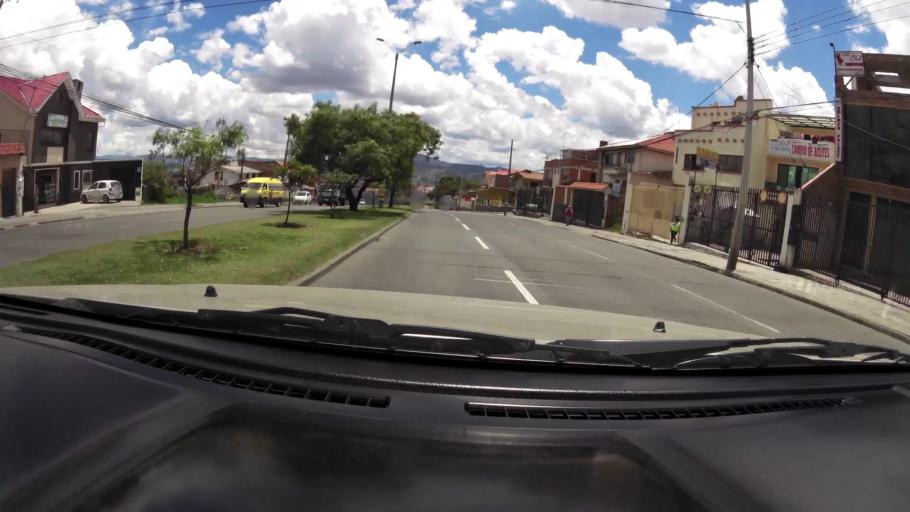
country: EC
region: Azuay
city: Cuenca
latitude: -2.8860
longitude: -78.9970
